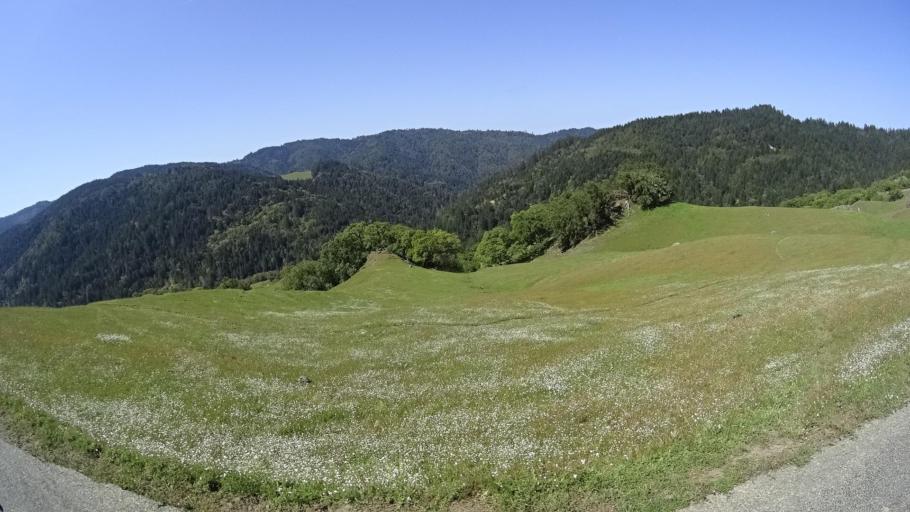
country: US
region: California
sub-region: Humboldt County
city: Redway
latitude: 40.0258
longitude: -123.6320
